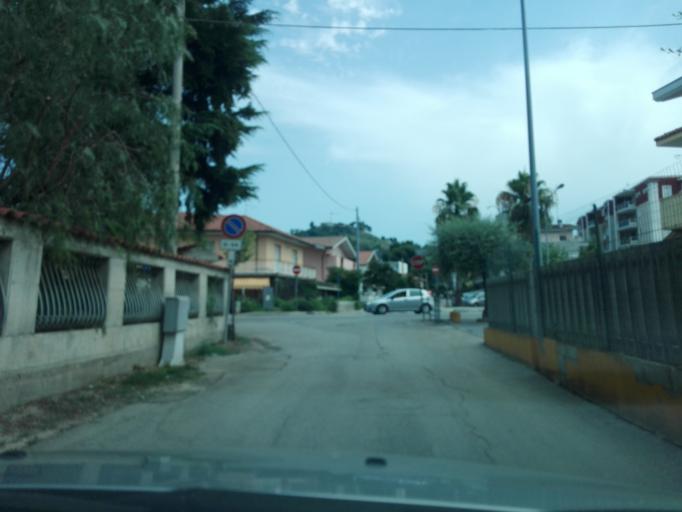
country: IT
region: Abruzzo
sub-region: Provincia di Pescara
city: Montesilvano Marina
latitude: 42.4987
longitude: 14.1301
